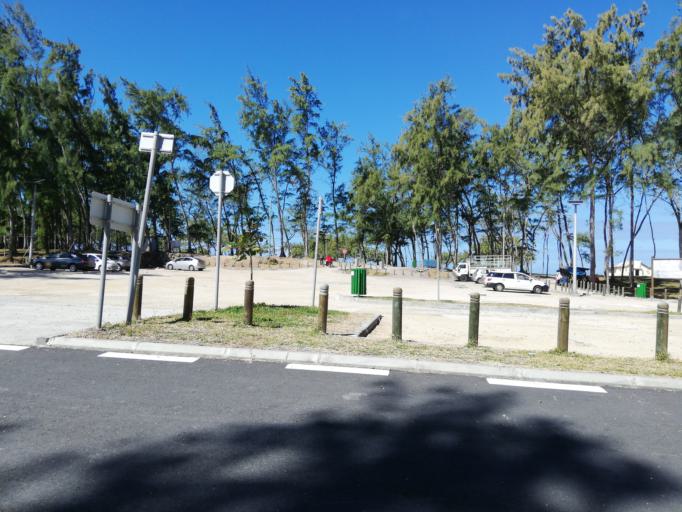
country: MU
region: Grand Port
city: Beau Vallon
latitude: -20.4535
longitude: 57.6978
